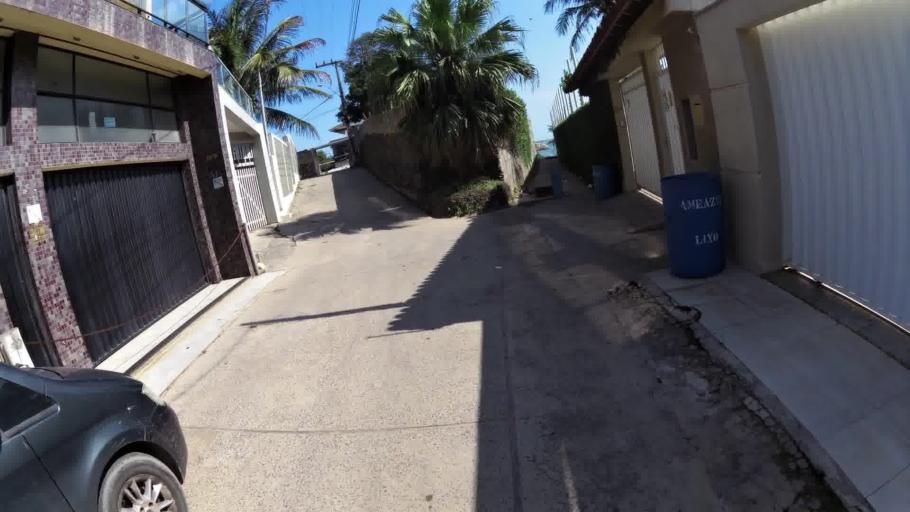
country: BR
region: Espirito Santo
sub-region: Guarapari
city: Guarapari
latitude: -20.7291
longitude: -40.5227
